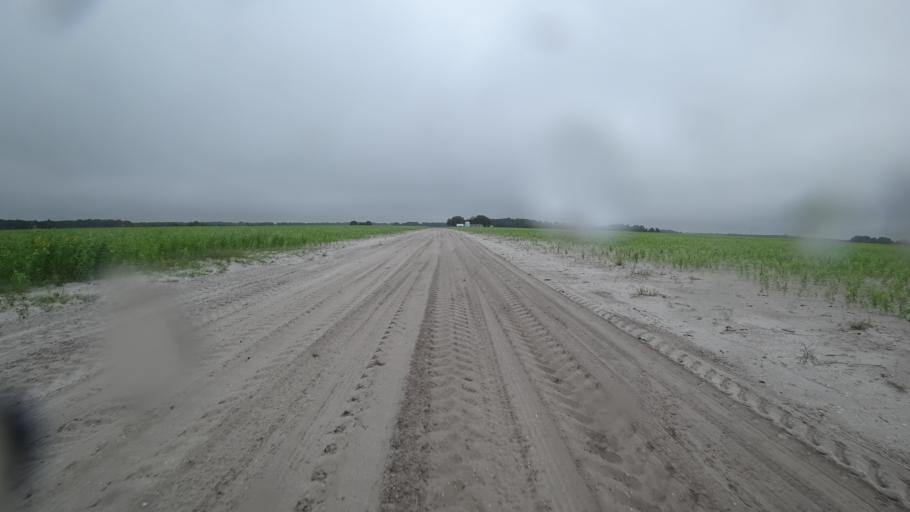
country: US
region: Florida
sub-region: Sarasota County
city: Warm Mineral Springs
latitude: 27.2952
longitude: -82.1609
